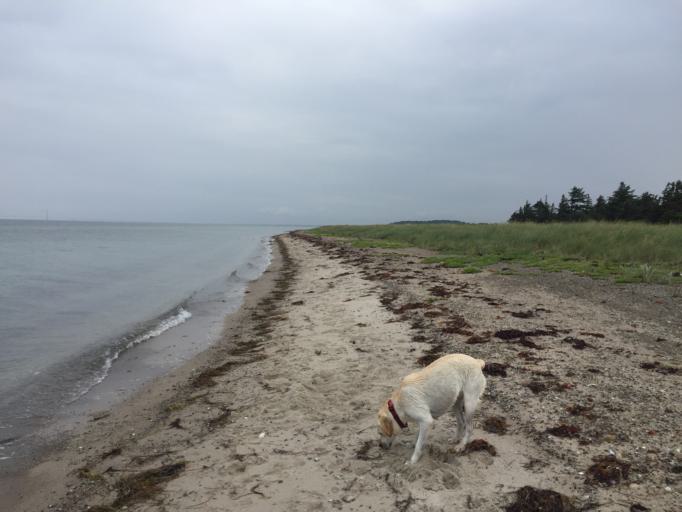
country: DK
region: Zealand
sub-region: Slagelse Kommune
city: Korsor
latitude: 55.2294
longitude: 11.1712
